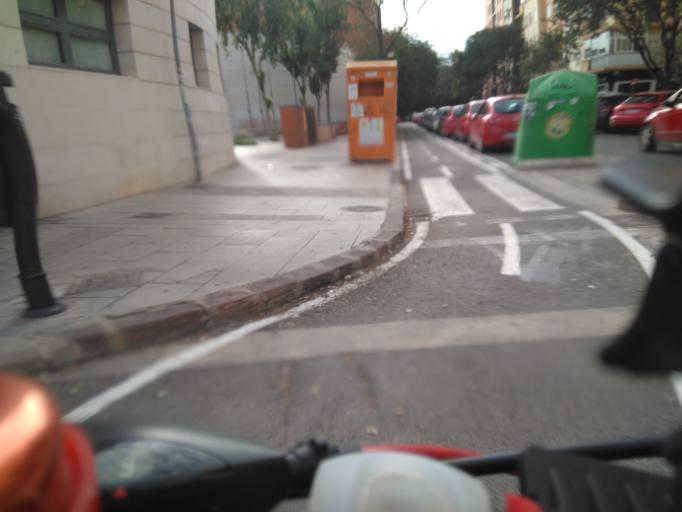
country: ES
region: Valencia
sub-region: Provincia de Valencia
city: Valencia
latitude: 39.4832
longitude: -0.3702
